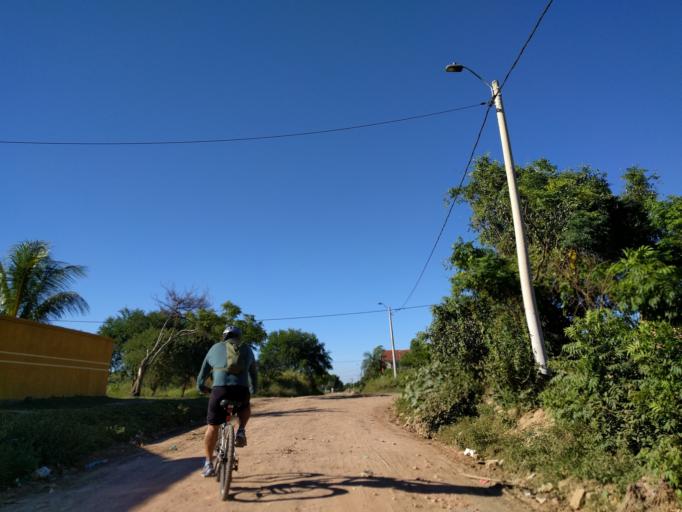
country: BO
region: Santa Cruz
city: Santa Cruz de la Sierra
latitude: -17.8470
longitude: -63.2379
